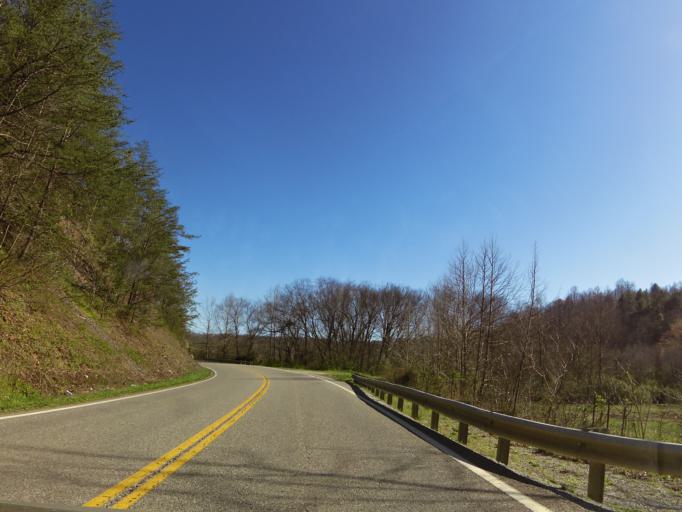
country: US
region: Tennessee
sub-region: Scott County
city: Huntsville
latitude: 36.4580
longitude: -84.4758
